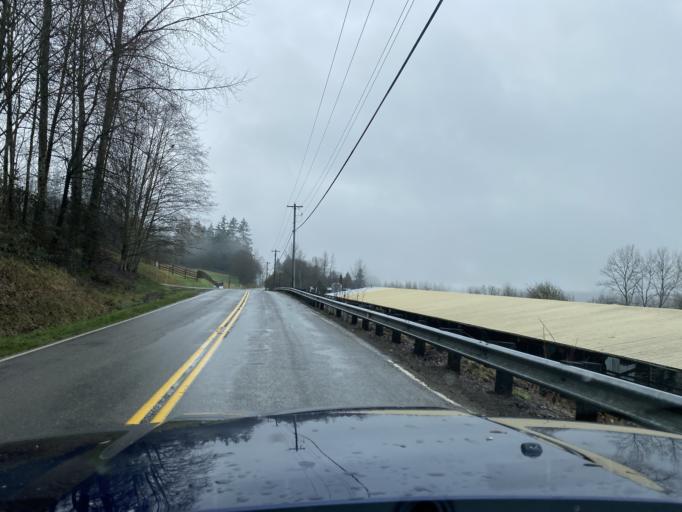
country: US
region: Washington
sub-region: King County
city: Duvall
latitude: 47.7905
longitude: -122.0010
